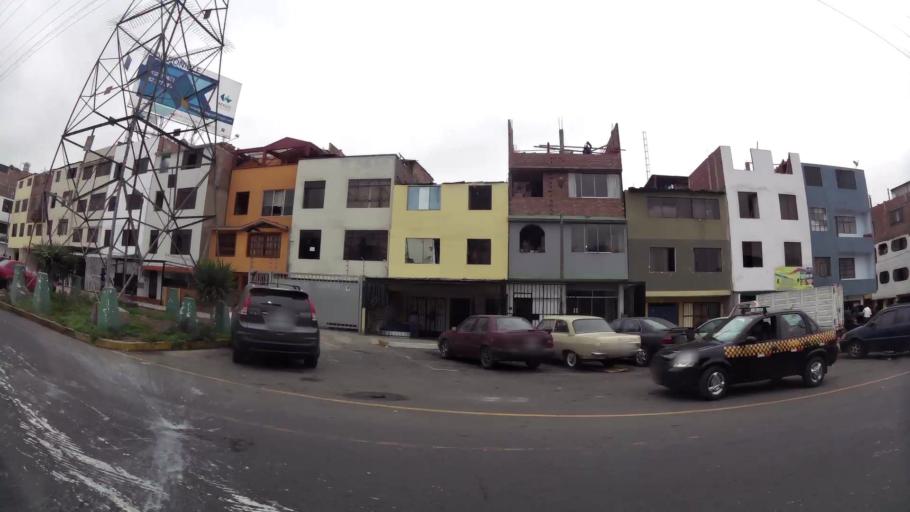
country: PE
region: Lima
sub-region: Lima
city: San Luis
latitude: -12.1079
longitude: -76.9919
